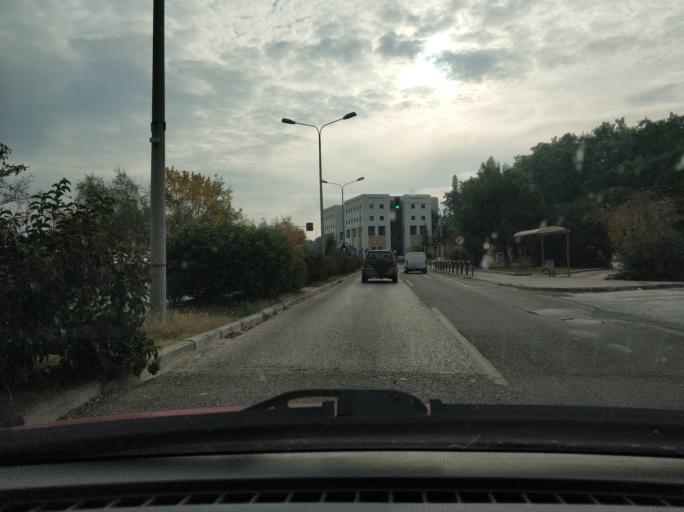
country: GR
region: East Macedonia and Thrace
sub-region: Nomos Kavalas
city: Kavala
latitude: 40.9318
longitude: 24.3924
